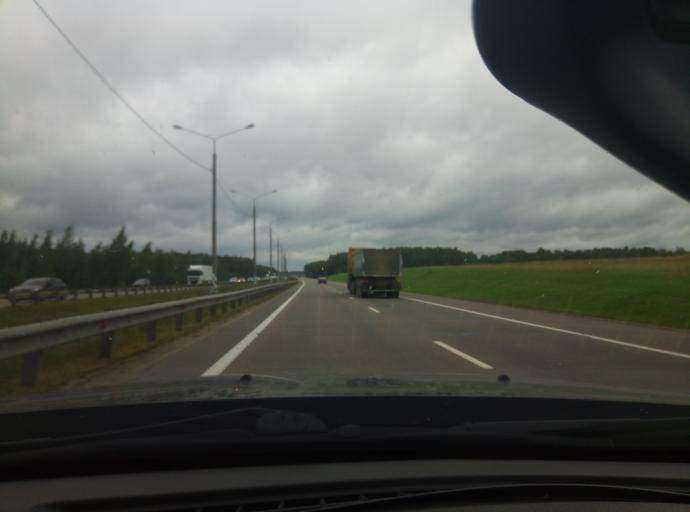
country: RU
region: Tula
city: Zaokskiy
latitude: 54.6785
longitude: 37.5062
